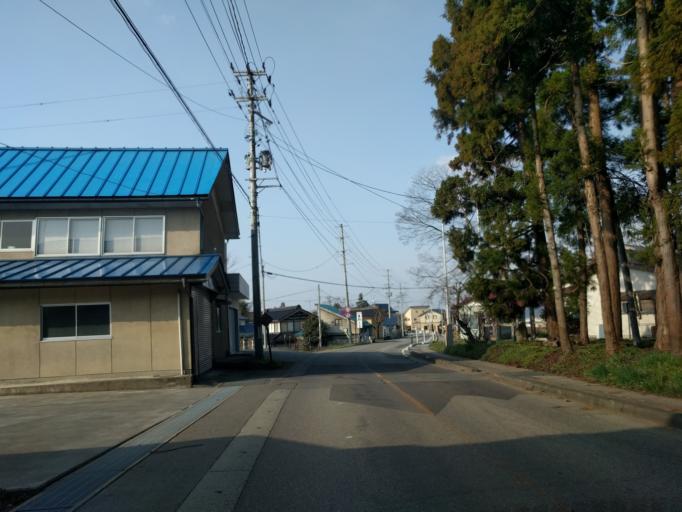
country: JP
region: Fukushima
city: Kitakata
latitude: 37.6663
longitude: 139.8852
